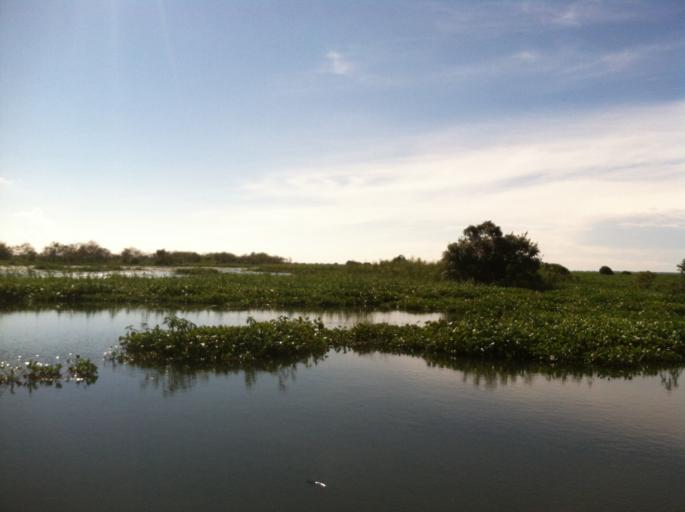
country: BD
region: Sylhet
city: Baniachang
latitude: 24.5900
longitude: 91.3586
